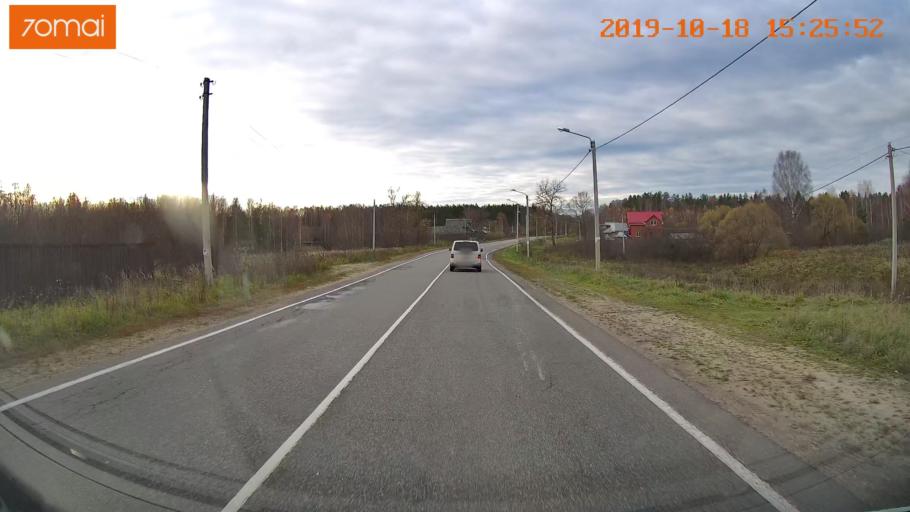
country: RU
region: Vladimir
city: Anopino
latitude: 55.7429
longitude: 40.6976
